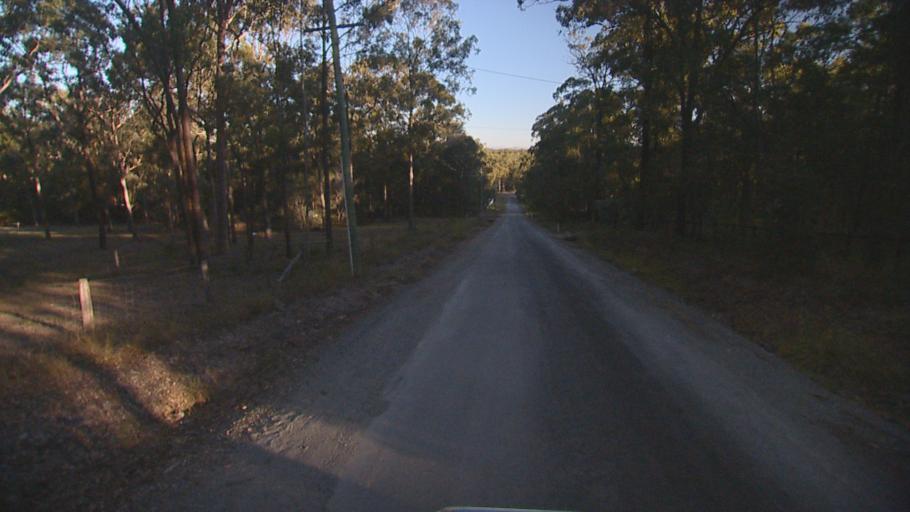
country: AU
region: Queensland
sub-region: Logan
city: Chambers Flat
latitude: -27.7663
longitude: 153.1329
